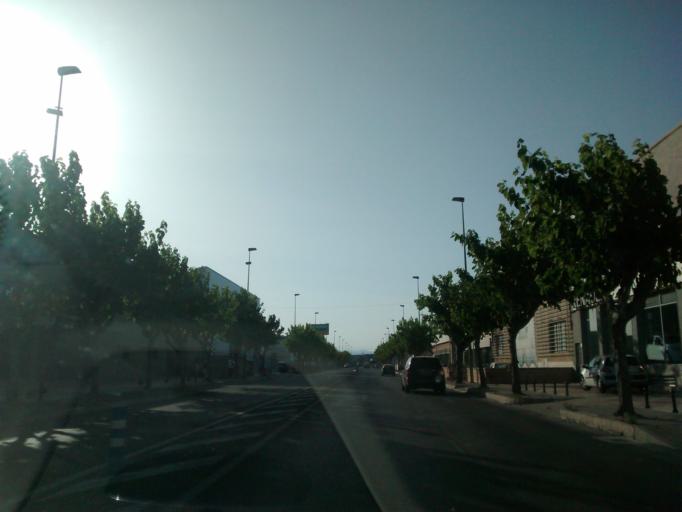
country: ES
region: Valencia
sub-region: Provincia de Alicante
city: Santa Pola
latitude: 38.1977
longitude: -0.5642
